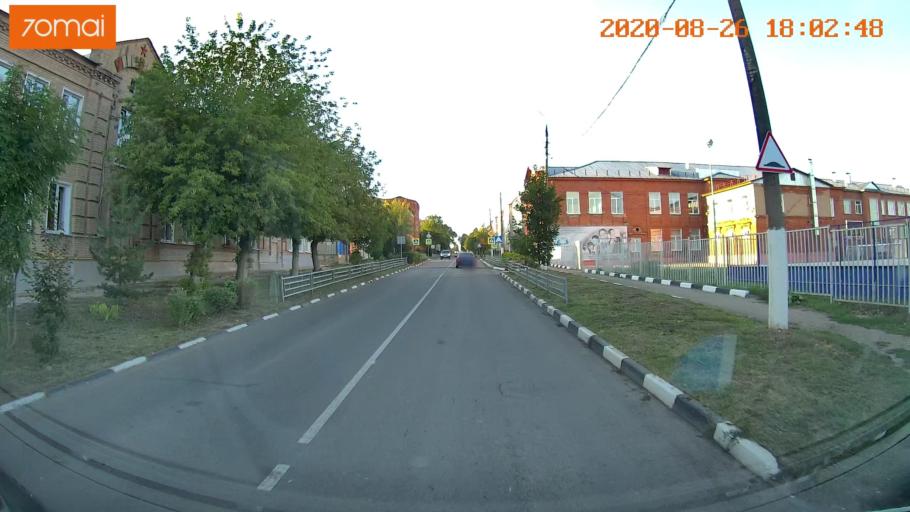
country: RU
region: Tula
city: Yefremov
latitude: 53.1408
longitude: 38.1208
